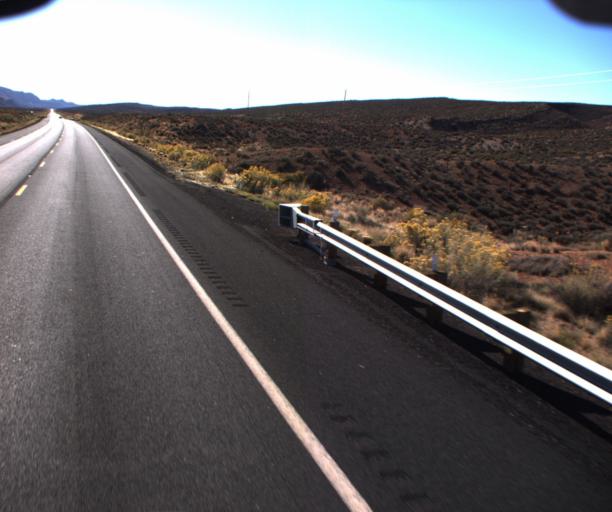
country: US
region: Arizona
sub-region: Coconino County
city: Tuba City
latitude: 36.2835
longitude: -111.4441
